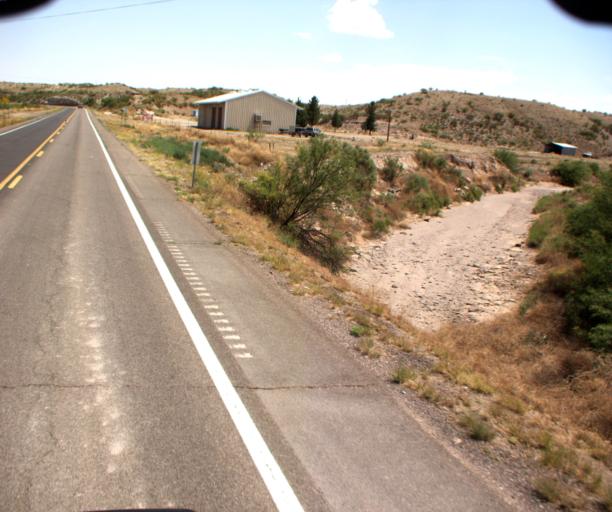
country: US
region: Arizona
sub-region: Greenlee County
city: Clifton
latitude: 32.7384
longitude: -109.1254
